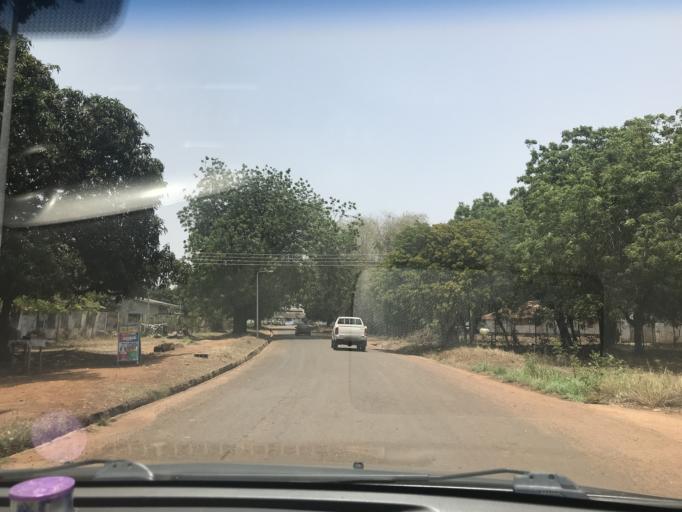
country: GH
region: Greater Accra
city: Teshi Old Town
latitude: 5.5836
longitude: -0.1538
